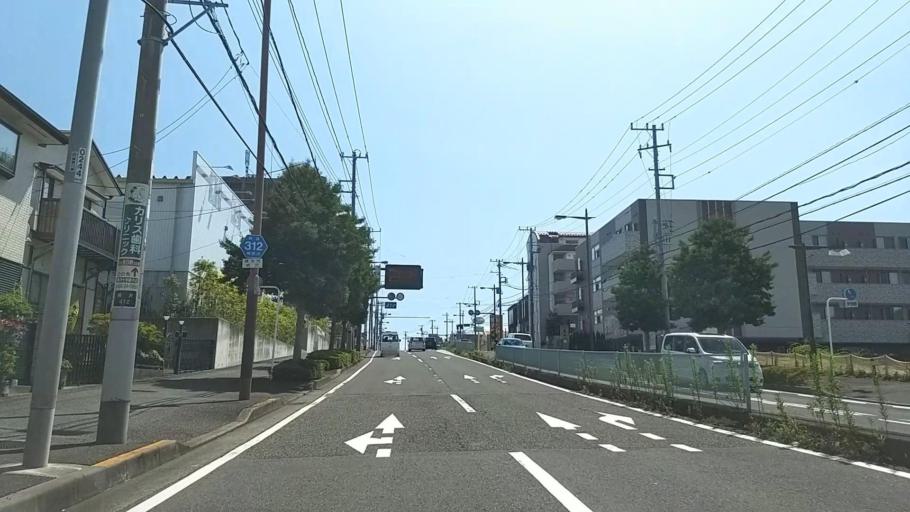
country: JP
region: Kanagawa
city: Fujisawa
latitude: 35.3557
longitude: 139.5031
